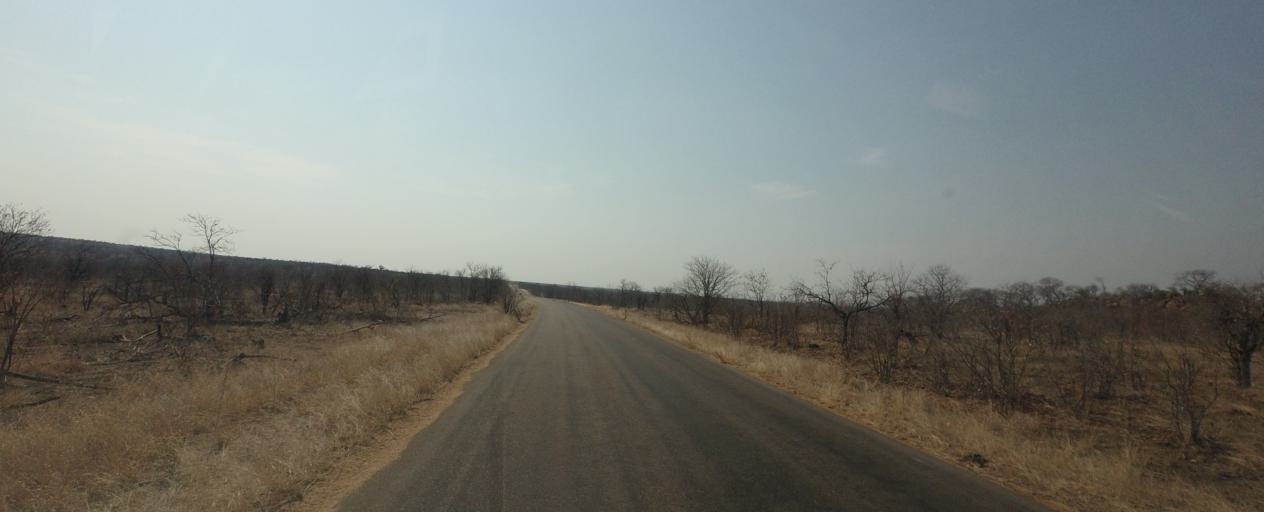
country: ZA
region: Limpopo
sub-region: Mopani District Municipality
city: Phalaborwa
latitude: -23.9539
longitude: 31.6220
